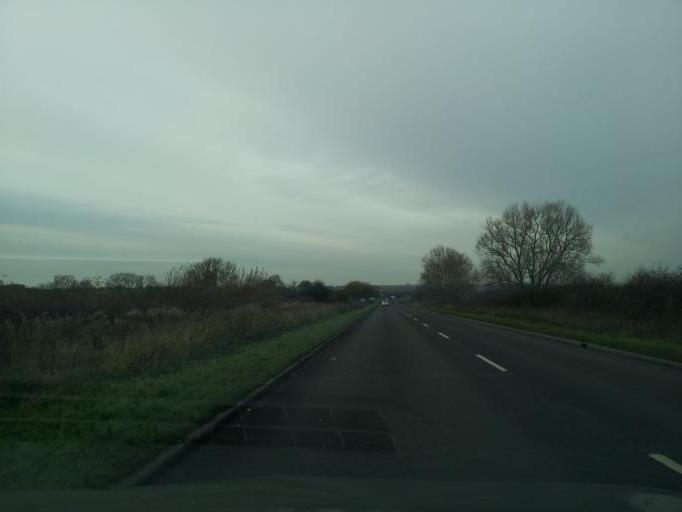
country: GB
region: England
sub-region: Buckinghamshire
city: Aylesbury
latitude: 51.8401
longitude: -0.7729
